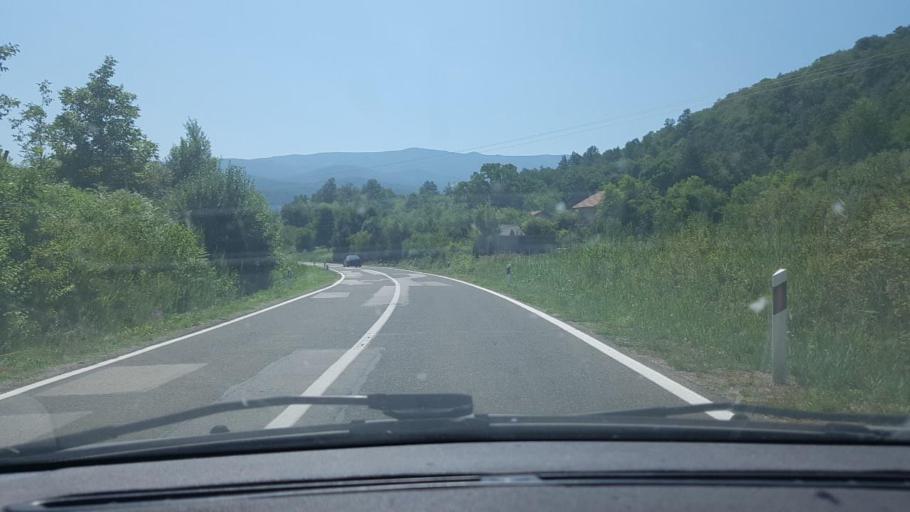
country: BA
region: Federation of Bosnia and Herzegovina
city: Bihac
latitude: 44.7536
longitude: 15.9423
